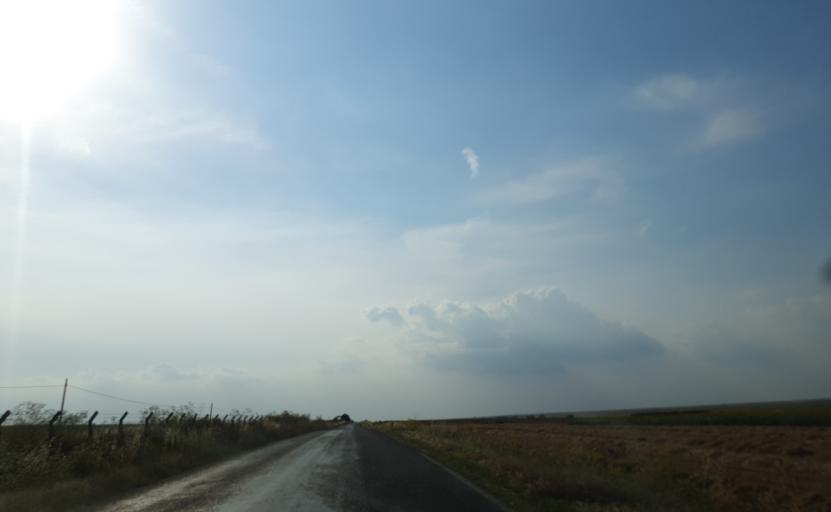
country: TR
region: Tekirdag
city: Muratli
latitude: 41.2064
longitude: 27.4587
